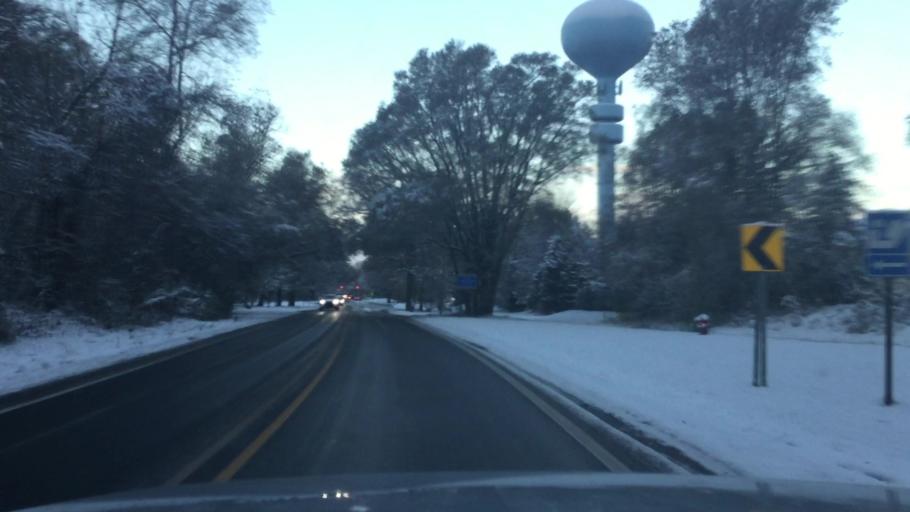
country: US
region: Michigan
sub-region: Oakland County
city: West Bloomfield Township
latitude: 42.5920
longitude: -83.4268
